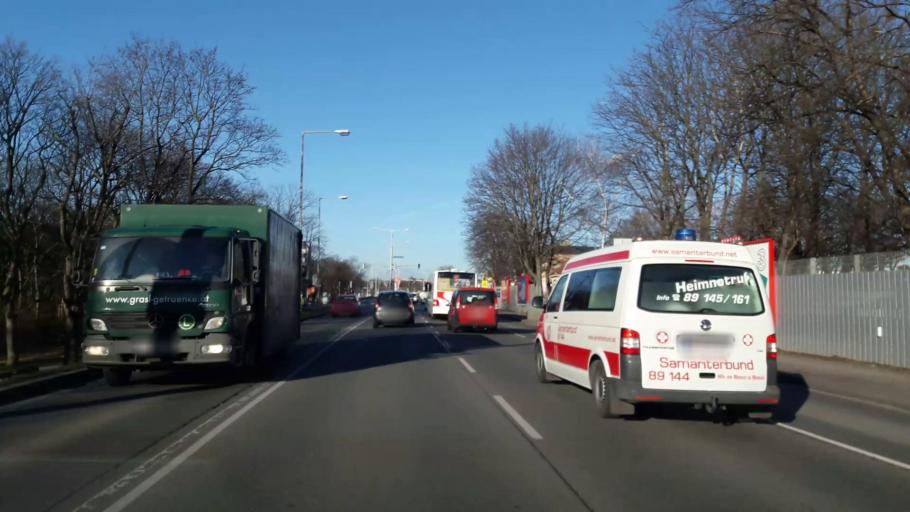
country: AT
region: Lower Austria
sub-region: Politischer Bezirk Wien-Umgebung
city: Leopoldsdorf
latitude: 48.1582
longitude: 16.3885
